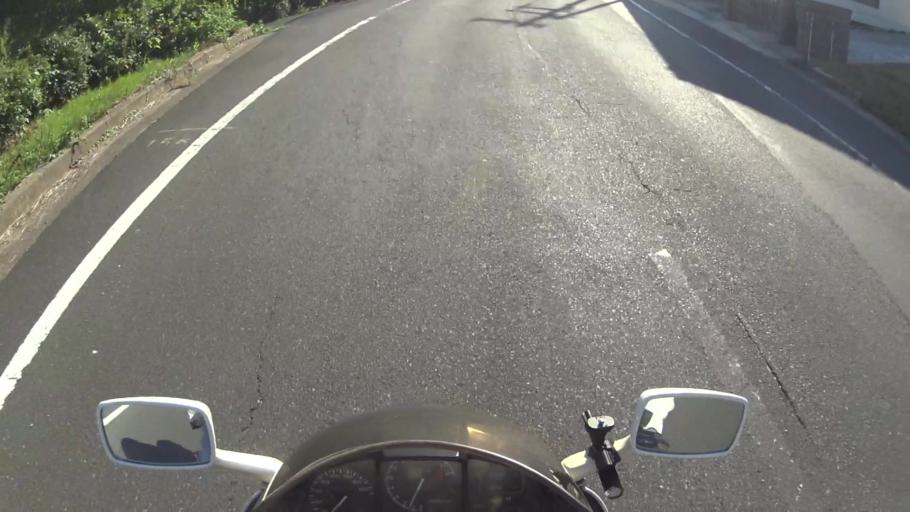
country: JP
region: Hyogo
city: Toyooka
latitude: 35.6389
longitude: 134.9437
